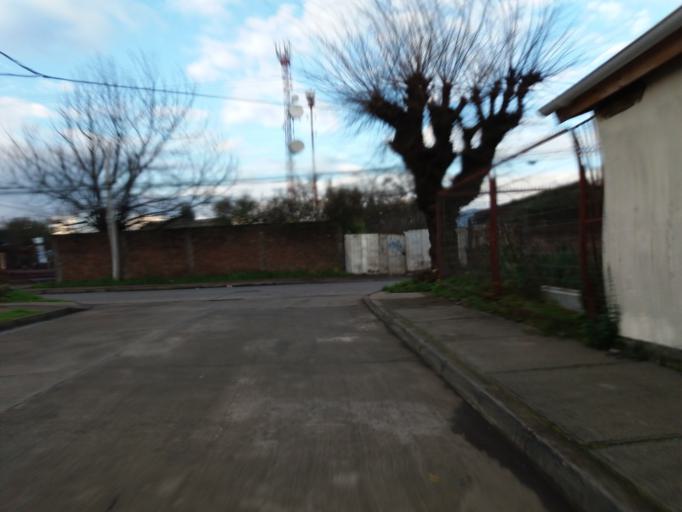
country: CL
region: Araucania
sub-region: Provincia de Cautin
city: Temuco
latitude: -38.7495
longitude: -72.6056
